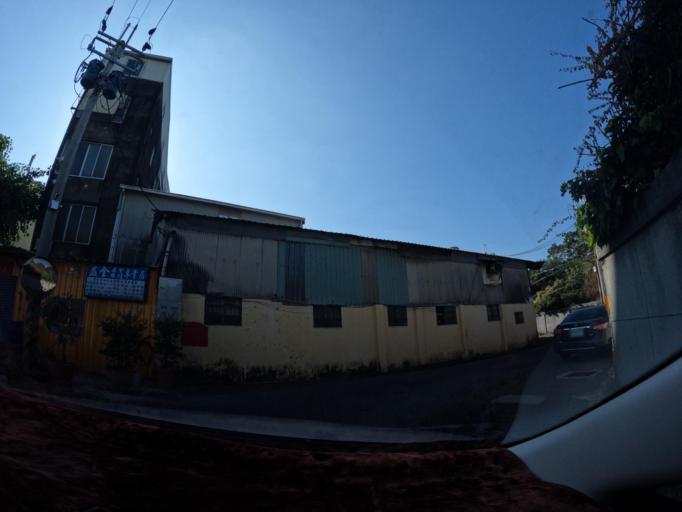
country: TW
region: Taiwan
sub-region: Tainan
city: Tainan
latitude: 23.0213
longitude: 120.2460
